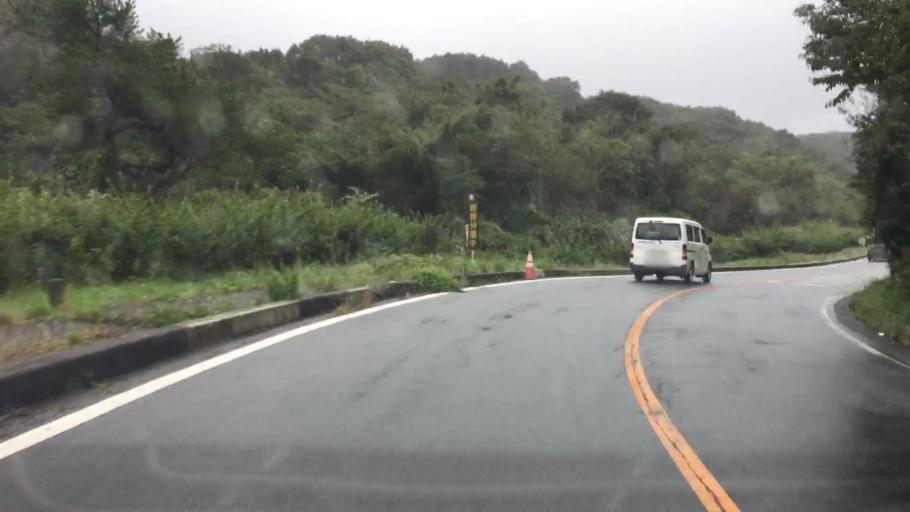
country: JP
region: Yamanashi
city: Fujikawaguchiko
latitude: 35.4280
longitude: 138.6295
